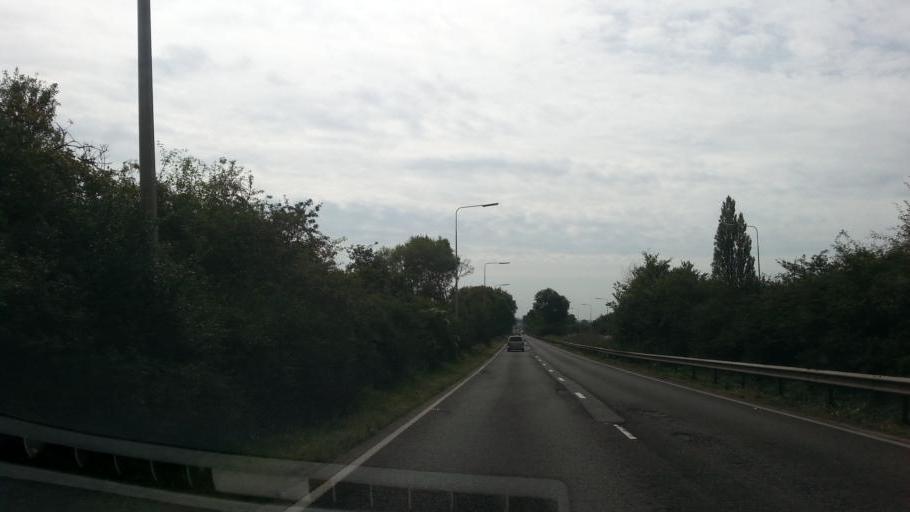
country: GB
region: England
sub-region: Central Bedfordshire
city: Astwick
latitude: 52.0421
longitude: -0.2229
